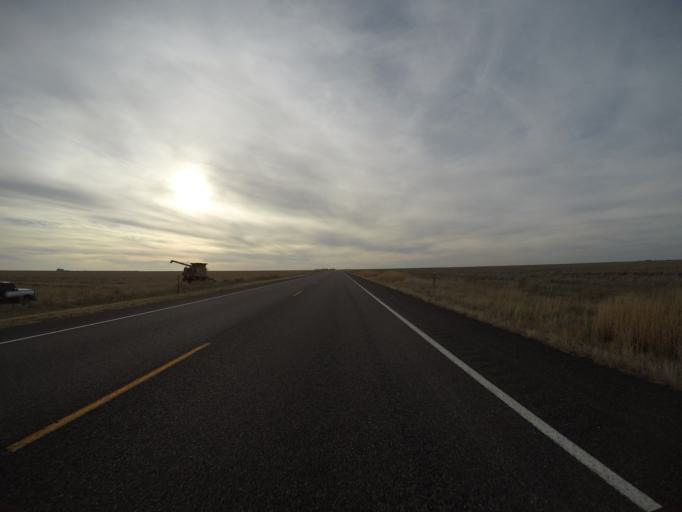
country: US
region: Colorado
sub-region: Yuma County
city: Wray
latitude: 39.7460
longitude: -102.1471
